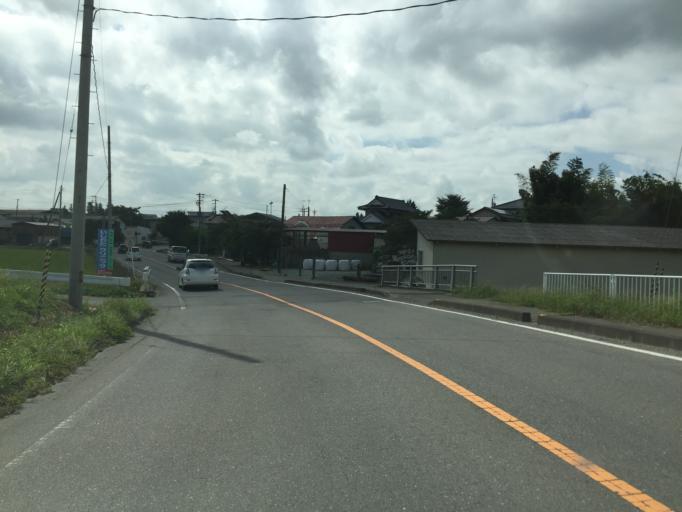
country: JP
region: Fukushima
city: Motomiya
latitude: 37.5017
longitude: 140.3780
